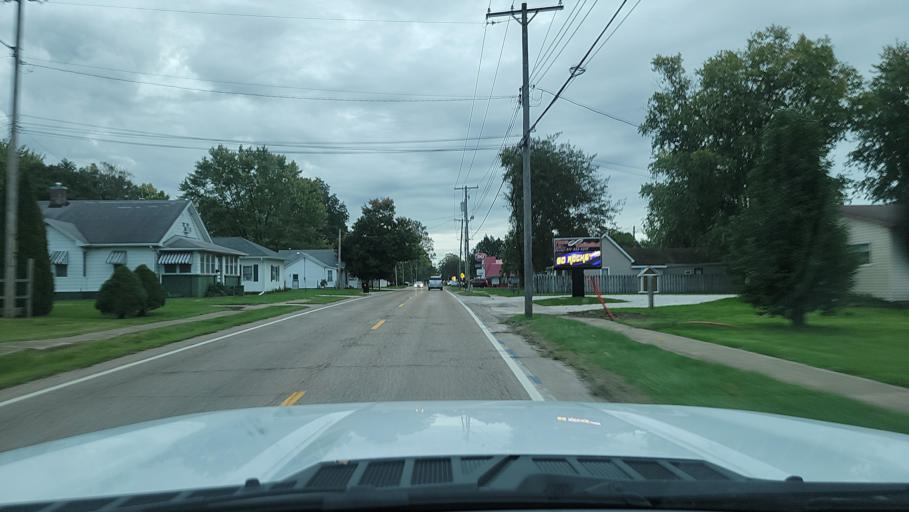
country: US
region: Illinois
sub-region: Schuyler County
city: Rushville
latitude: 40.1177
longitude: -90.5687
